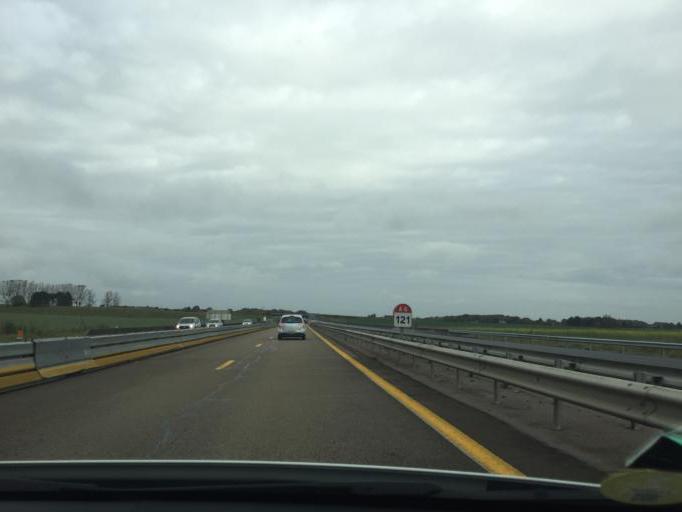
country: FR
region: Bourgogne
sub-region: Departement de l'Yonne
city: Saint-Julien-du-Sault
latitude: 47.9870
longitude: 3.1832
